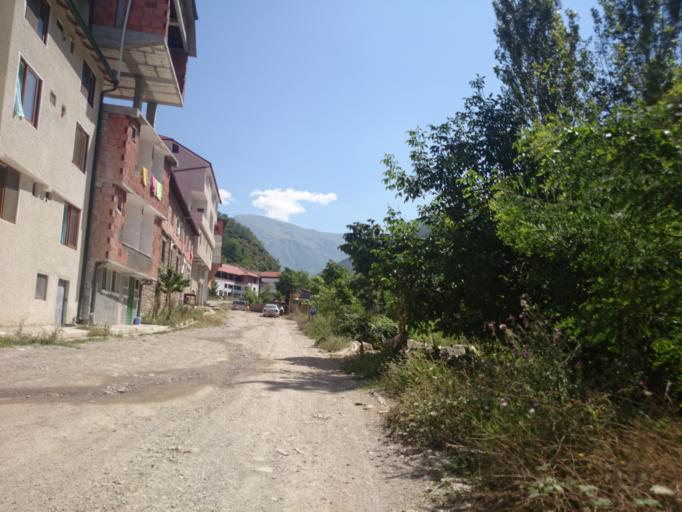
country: AL
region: Diber
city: Peshkopi
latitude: 41.6853
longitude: 20.4492
